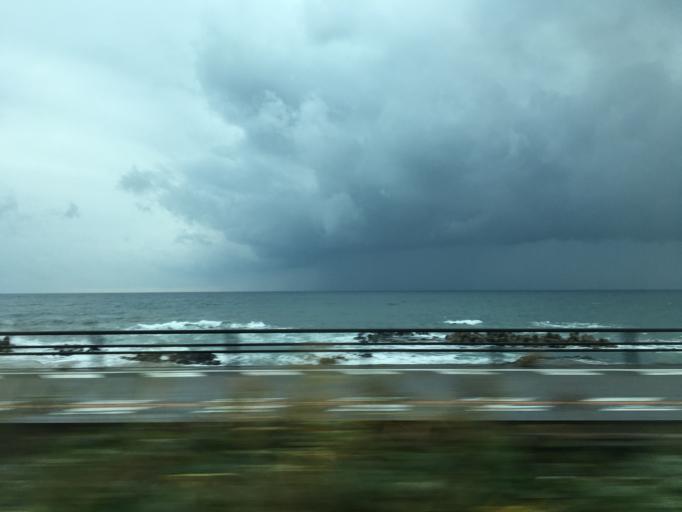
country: JP
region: Yamagata
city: Tsuruoka
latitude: 38.6153
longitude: 139.5795
